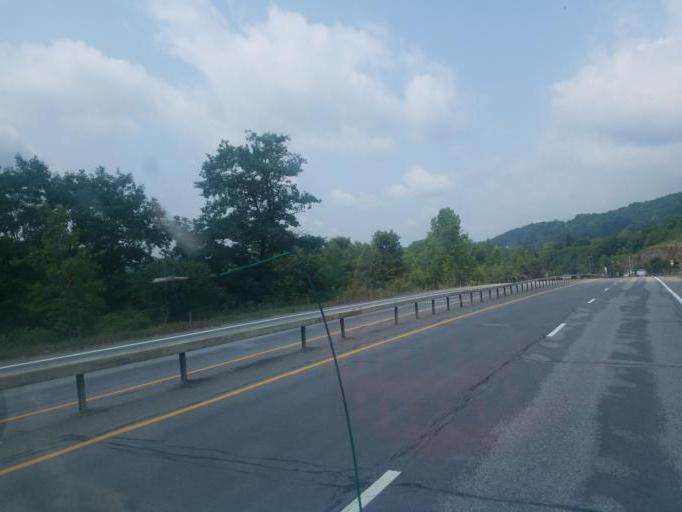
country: US
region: New York
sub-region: Herkimer County
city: Little Falls
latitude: 43.0411
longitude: -74.8433
